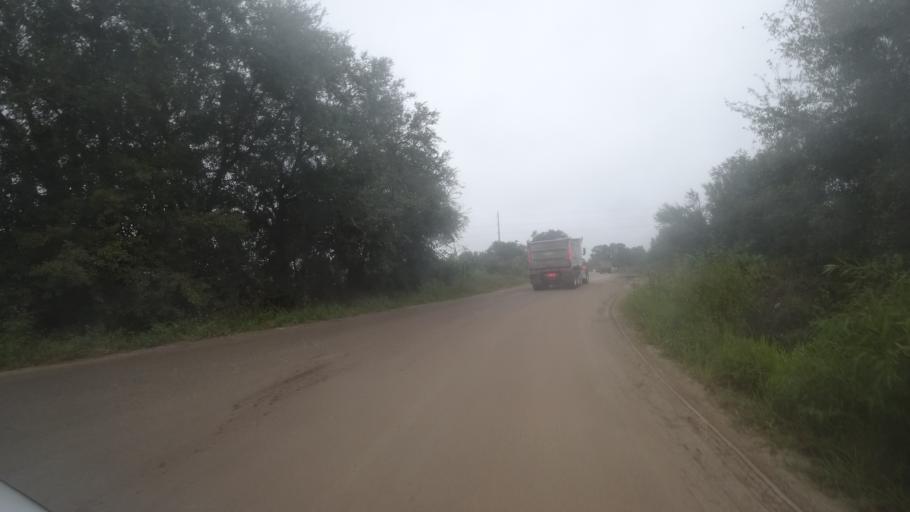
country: US
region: Florida
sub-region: Sarasota County
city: The Meadows
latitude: 27.4738
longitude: -82.3467
